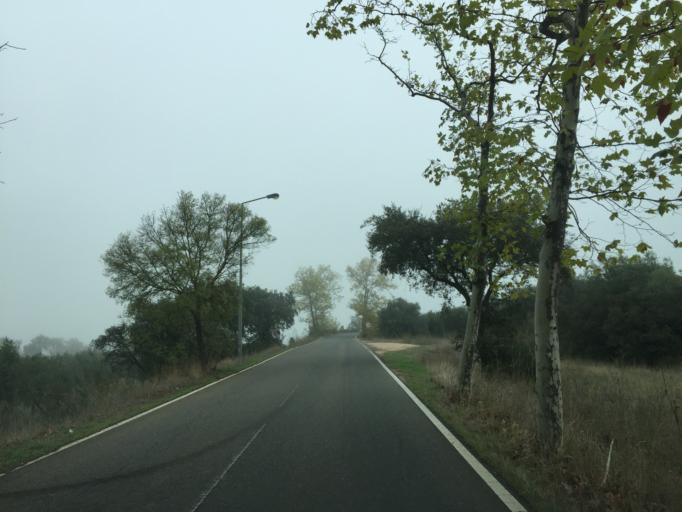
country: PT
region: Portalegre
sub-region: Alter do Chao
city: Alter do Chao
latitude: 39.1376
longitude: -7.5753
